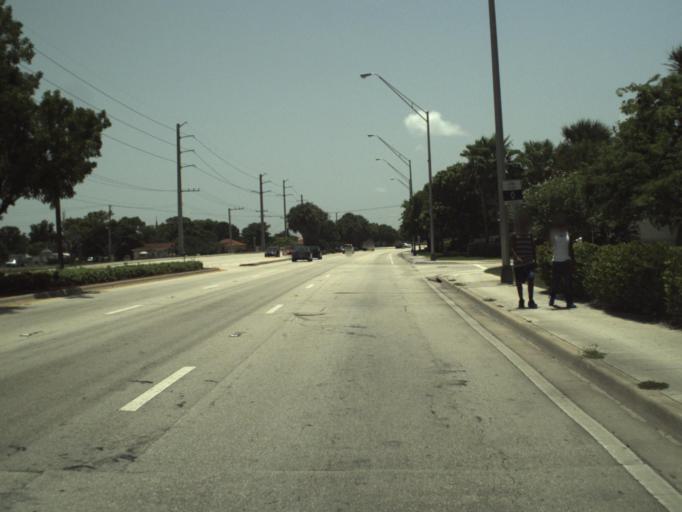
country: US
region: Florida
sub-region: Broward County
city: Pompano Beach
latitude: 26.2421
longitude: -80.1516
